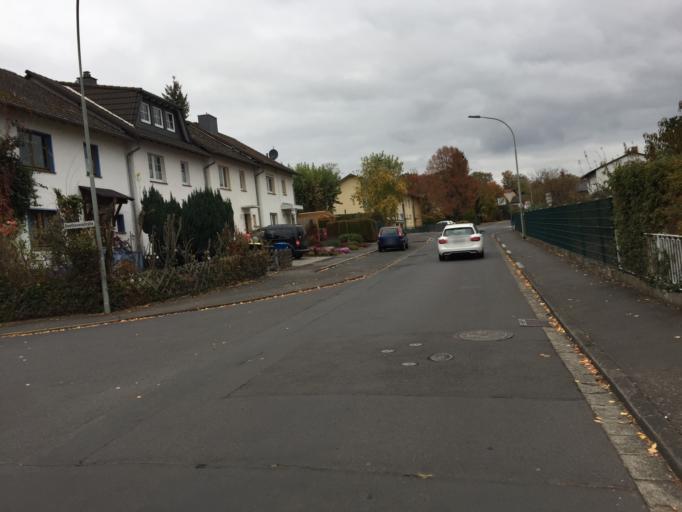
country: DE
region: Hesse
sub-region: Regierungsbezirk Giessen
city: Lich
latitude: 50.5200
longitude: 8.8093
